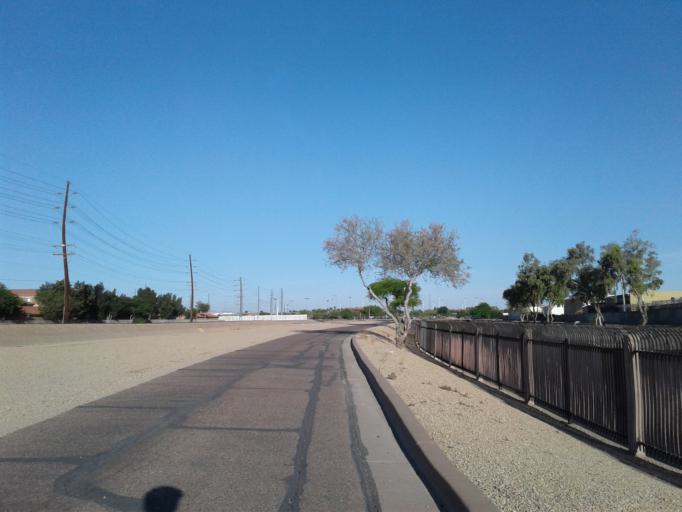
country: US
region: Arizona
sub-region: Maricopa County
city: Glendale
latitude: 33.5725
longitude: -112.1039
